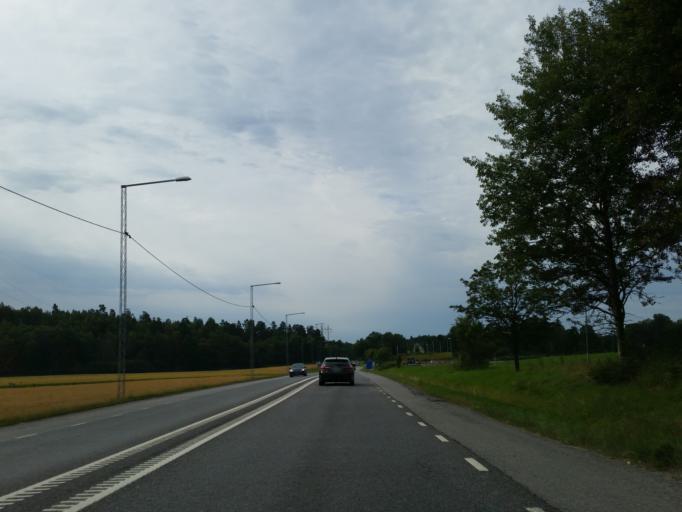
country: SE
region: Stockholm
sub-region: Botkyrka Kommun
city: Alby
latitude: 59.2247
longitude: 17.8378
